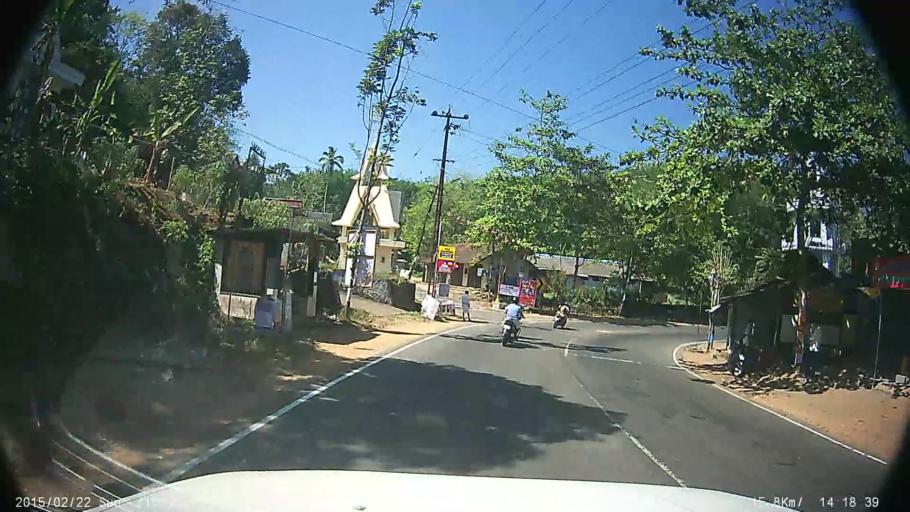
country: IN
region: Kerala
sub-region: Kottayam
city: Lalam
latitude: 9.5662
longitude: 76.6872
